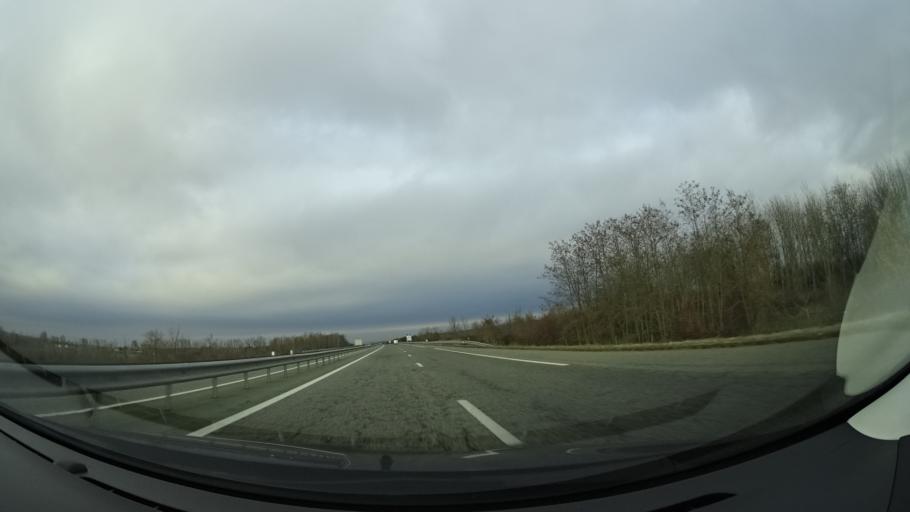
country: FR
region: Midi-Pyrenees
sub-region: Departement de l'Ariege
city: Pamiers
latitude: 43.1755
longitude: 1.6230
